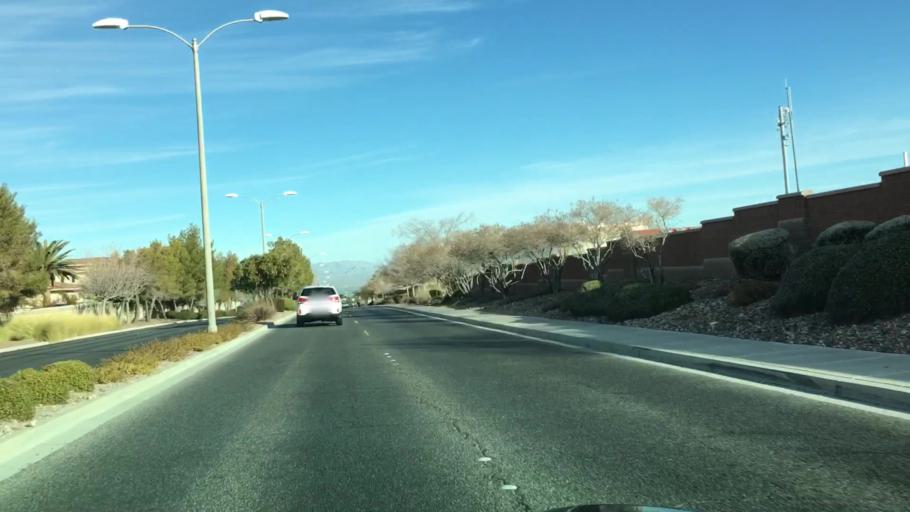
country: US
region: Nevada
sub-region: Clark County
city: Whitney
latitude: 35.9760
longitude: -115.1008
